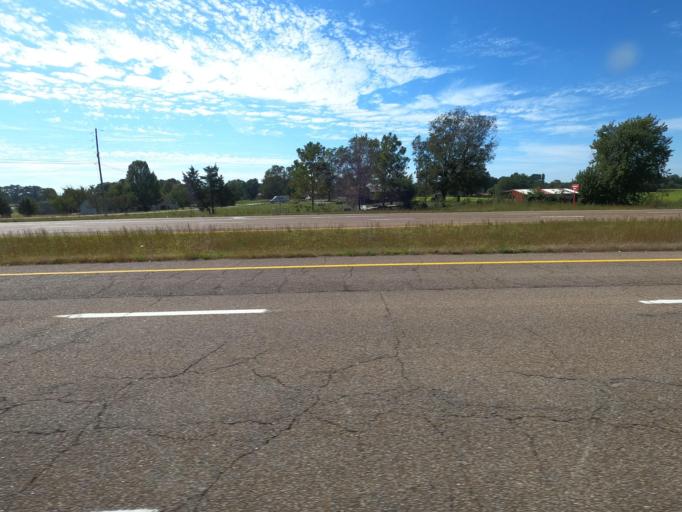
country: US
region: Tennessee
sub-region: Crockett County
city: Alamo
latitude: 35.7832
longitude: -89.1439
